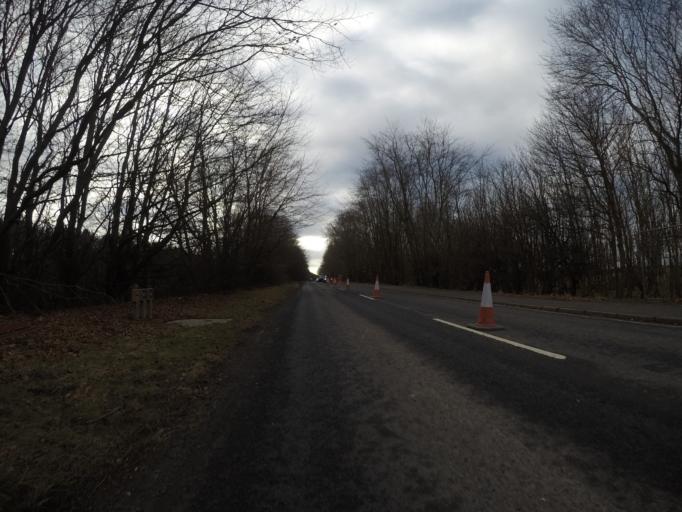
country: GB
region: Scotland
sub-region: North Ayrshire
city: Dreghorn
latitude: 55.5848
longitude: -4.6467
